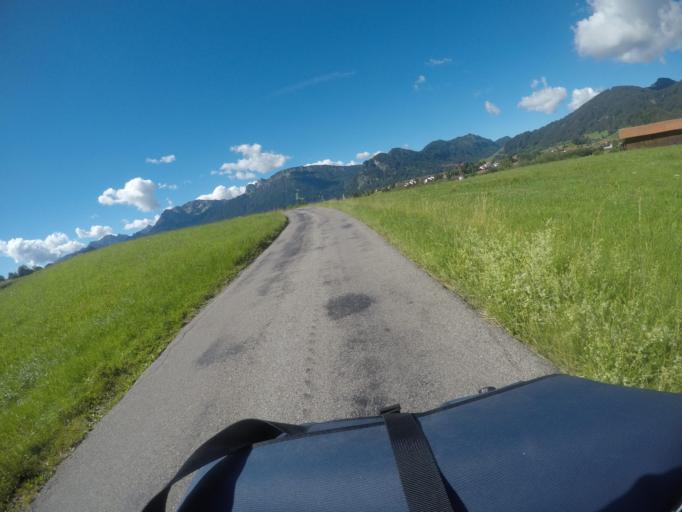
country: DE
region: Bavaria
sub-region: Swabia
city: Pfronten
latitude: 47.6014
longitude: 10.5655
